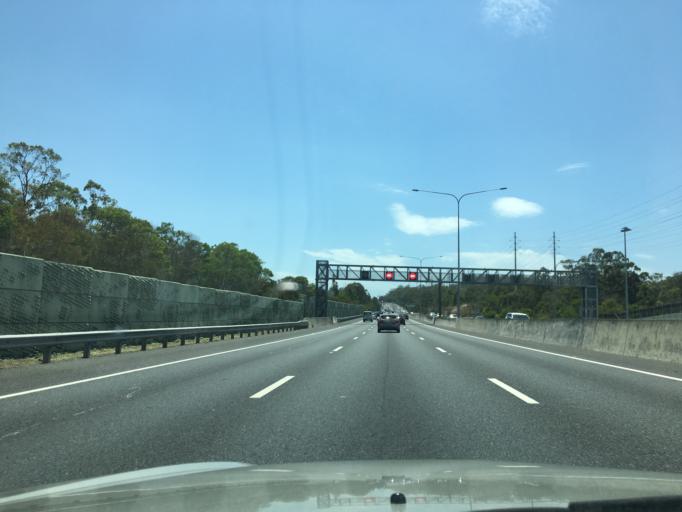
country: AU
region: Queensland
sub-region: Brisbane
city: Mackenzie
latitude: -27.5297
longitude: 153.1233
